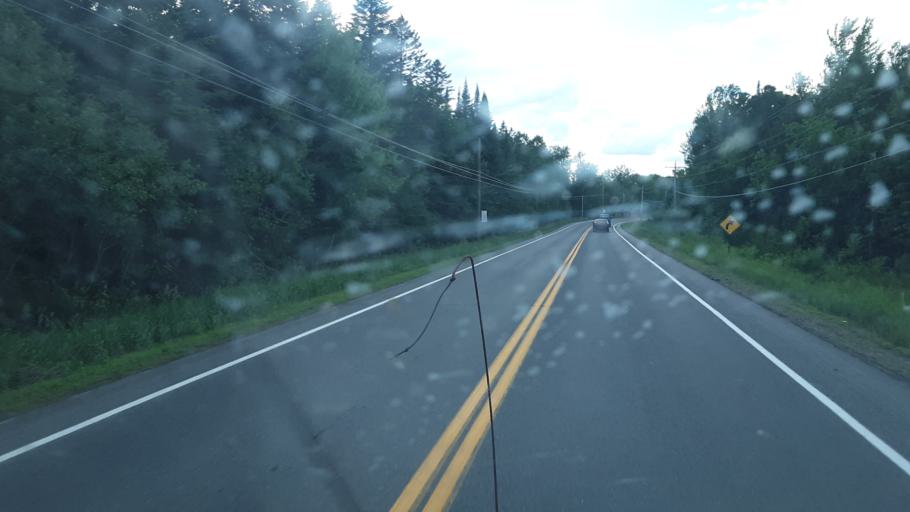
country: US
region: Maine
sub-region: Penobscot County
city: Patten
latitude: 45.9278
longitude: -68.4432
